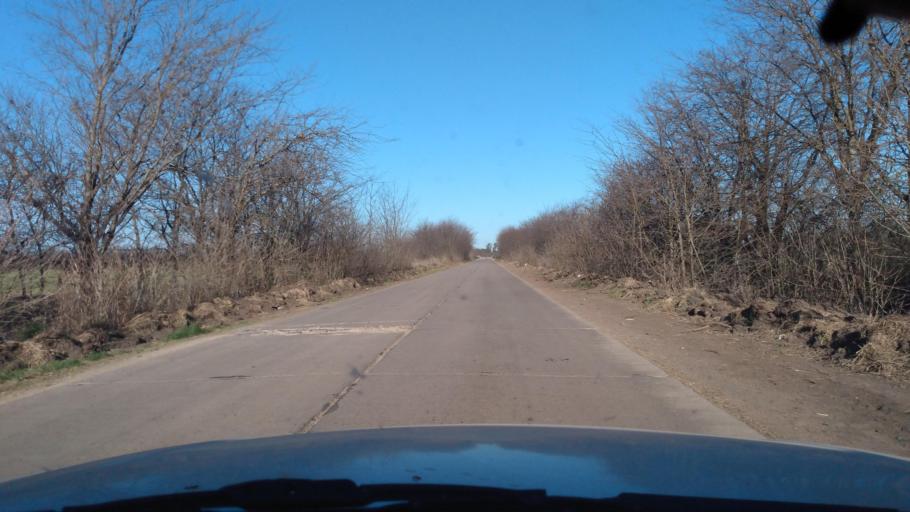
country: AR
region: Buenos Aires
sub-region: Partido de Lujan
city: Lujan
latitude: -34.6154
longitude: -59.2644
